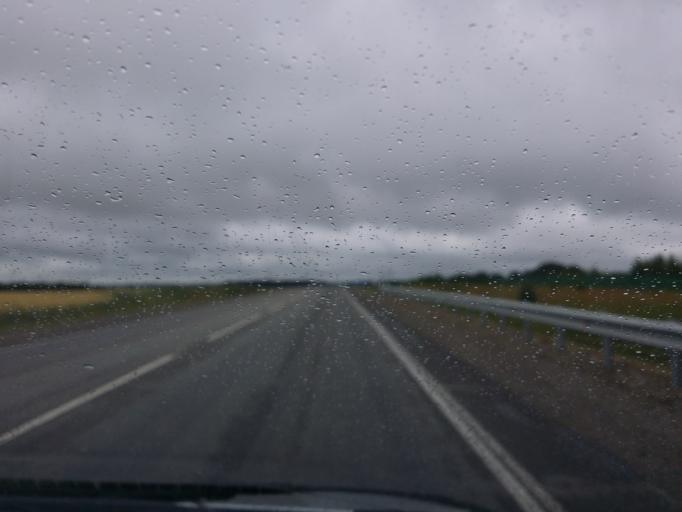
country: RU
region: Altai Krai
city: Nalobikha
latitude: 53.1235
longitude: 84.7140
